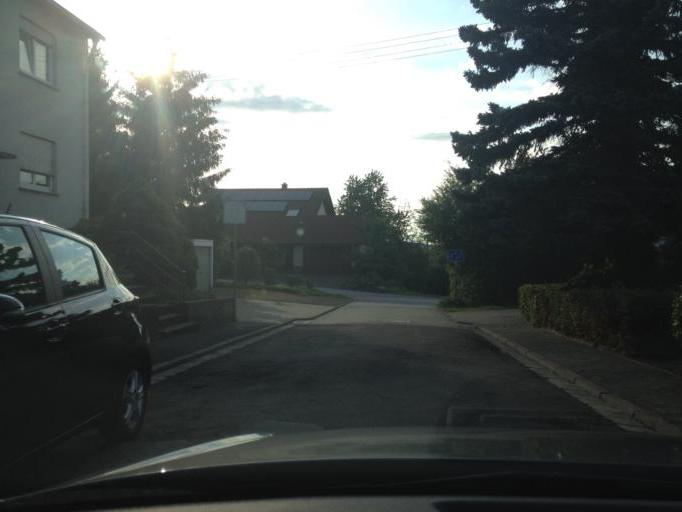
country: DE
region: Saarland
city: Sankt Wendel
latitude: 49.4577
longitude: 7.1685
